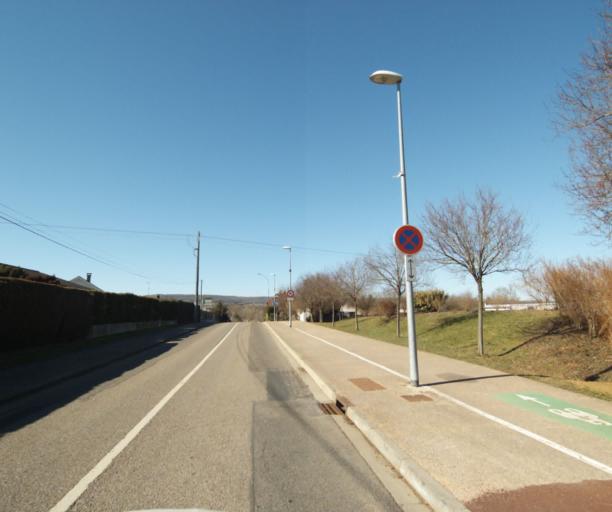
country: FR
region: Lorraine
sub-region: Departement de Meurthe-et-Moselle
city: Fleville-devant-Nancy
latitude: 48.6280
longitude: 6.2123
